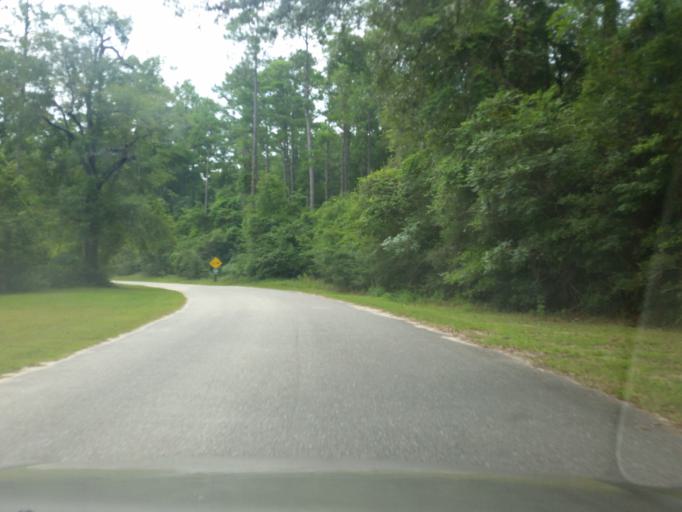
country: US
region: Alabama
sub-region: Baldwin County
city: Spanish Fort
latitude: 30.7410
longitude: -87.9097
